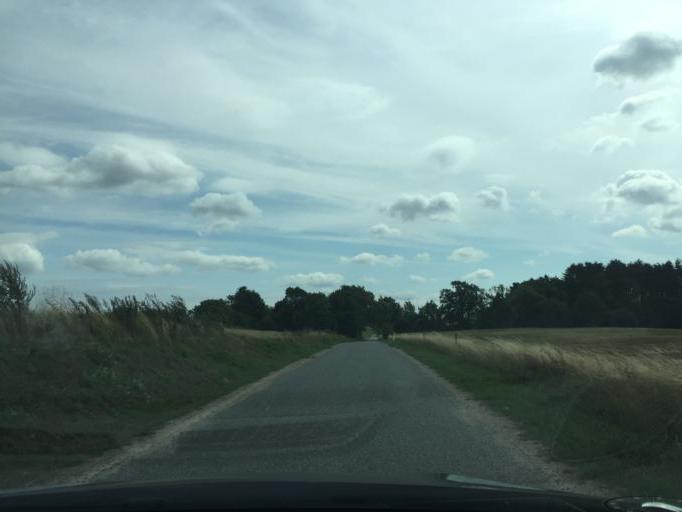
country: DK
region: South Denmark
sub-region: Assens Kommune
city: Tommerup Stationsby
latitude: 55.4011
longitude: 10.2365
